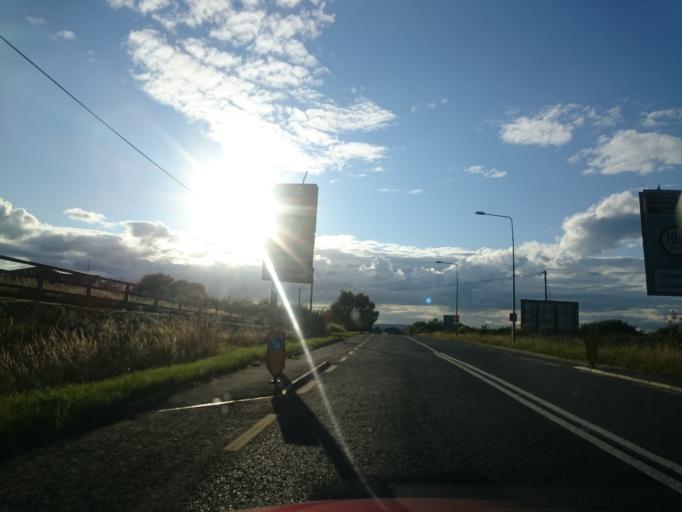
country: IE
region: Leinster
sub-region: Loch Garman
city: Rosslare
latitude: 52.2445
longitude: -6.3930
